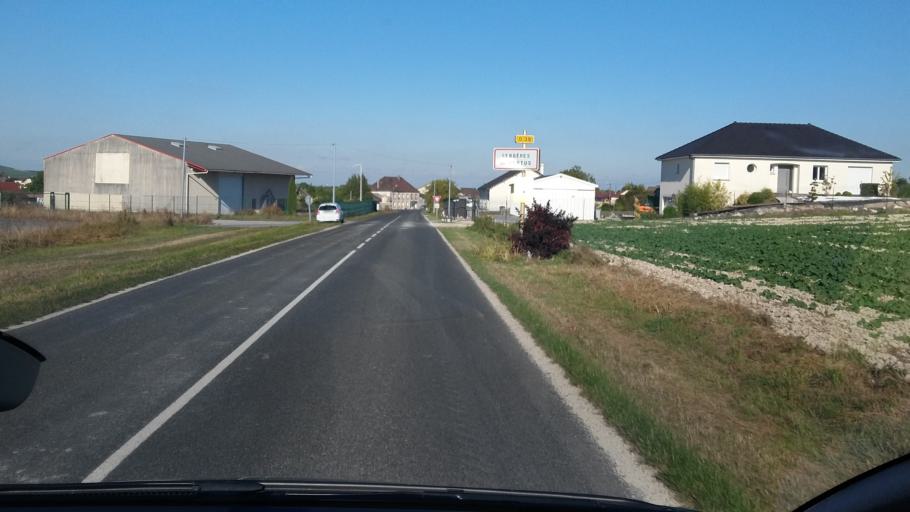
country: FR
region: Champagne-Ardenne
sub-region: Departement de la Marne
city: Vertus
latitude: 48.8739
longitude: 3.9970
